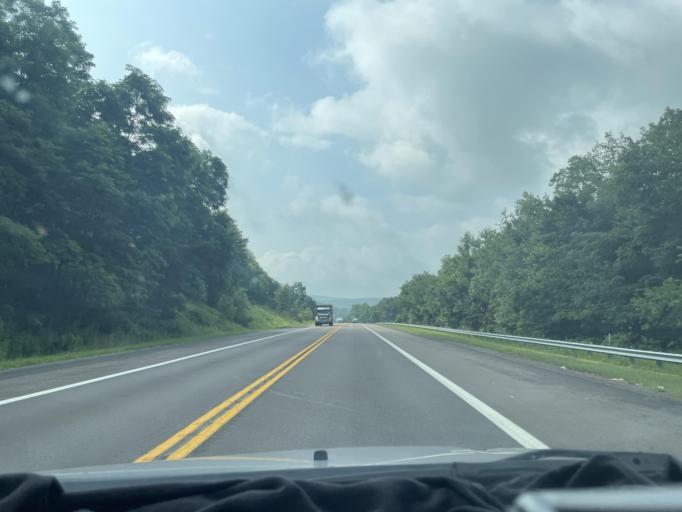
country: US
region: Maryland
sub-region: Garrett County
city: Oakland
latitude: 39.5433
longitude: -79.3503
